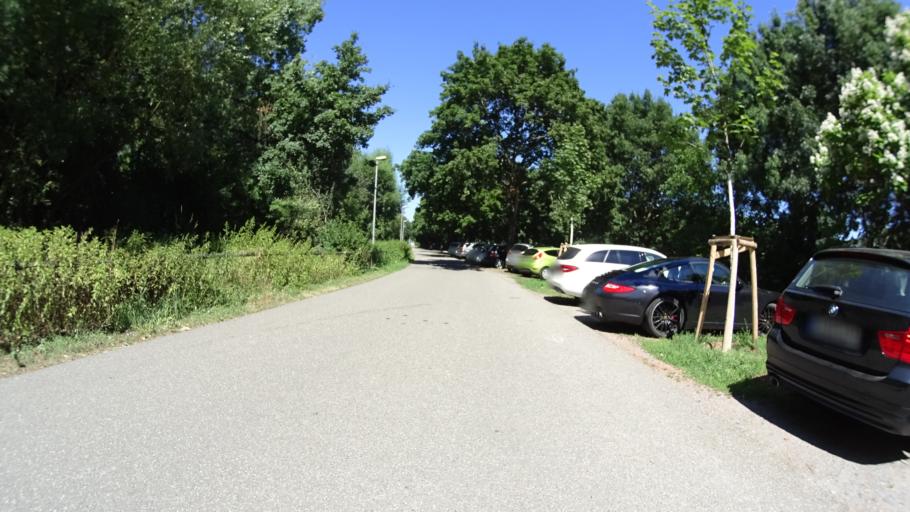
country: DE
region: Baden-Wuerttemberg
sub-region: Karlsruhe Region
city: Weingarten
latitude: 49.0041
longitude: 8.4810
